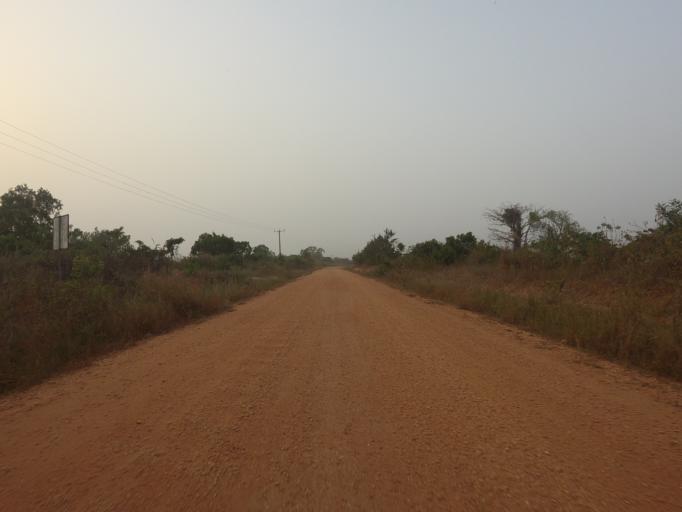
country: GH
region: Volta
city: Anloga
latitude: 5.9798
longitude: 0.6048
